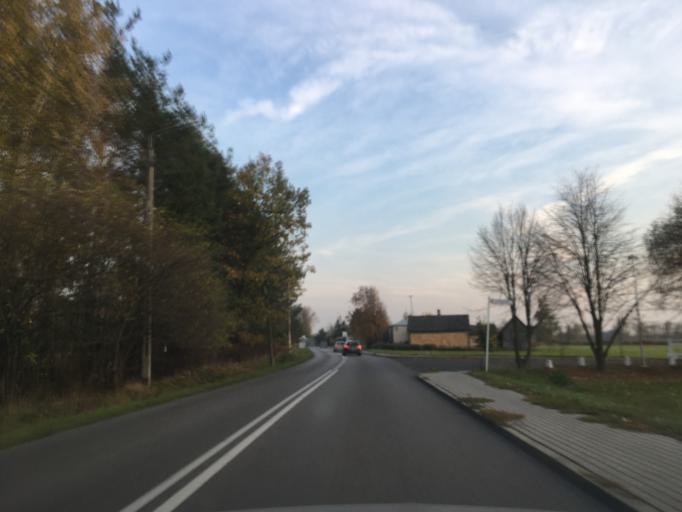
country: PL
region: Masovian Voivodeship
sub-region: Powiat piaseczynski
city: Lesznowola
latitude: 52.0558
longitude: 20.9234
